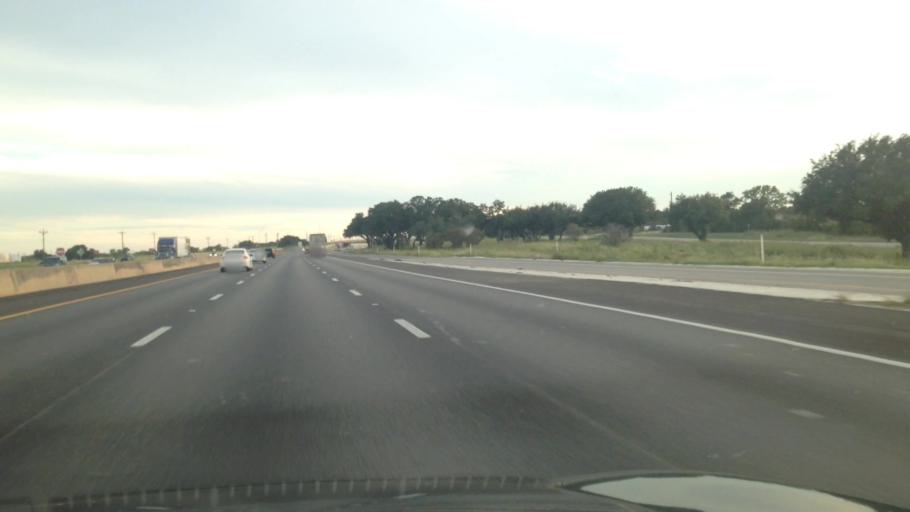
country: US
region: Texas
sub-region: Hays County
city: Kyle
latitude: 29.9547
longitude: -97.8779
